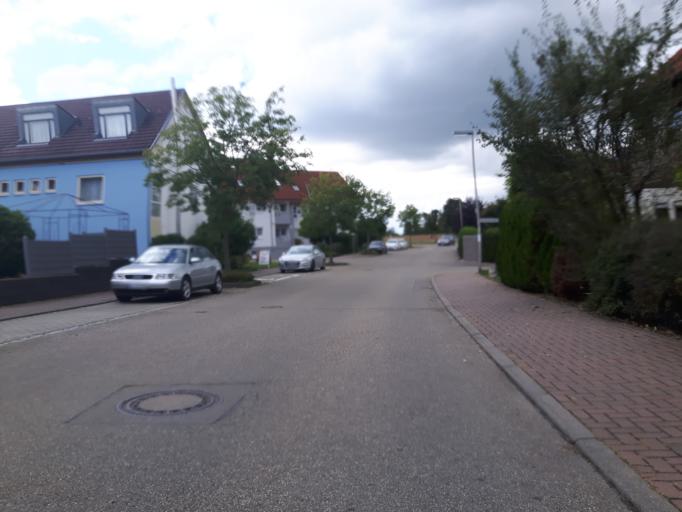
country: DE
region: Baden-Wuerttemberg
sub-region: Regierungsbezirk Stuttgart
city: Bad Wimpfen
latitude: 49.2246
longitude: 9.1503
